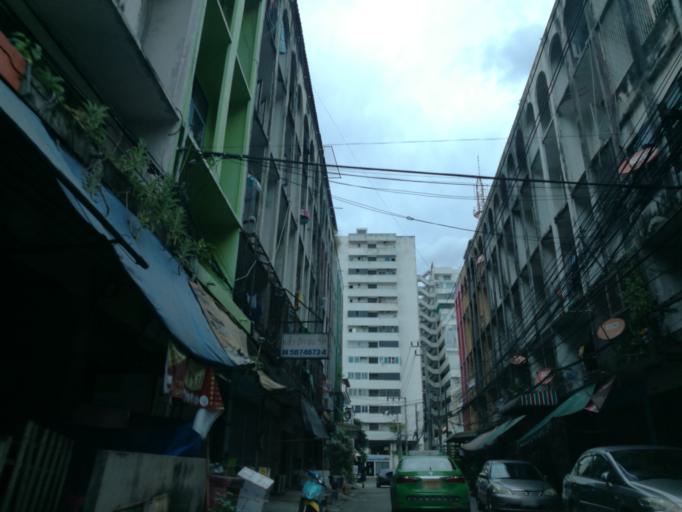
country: TH
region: Bangkok
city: Bang Sue
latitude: 13.8001
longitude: 100.5361
